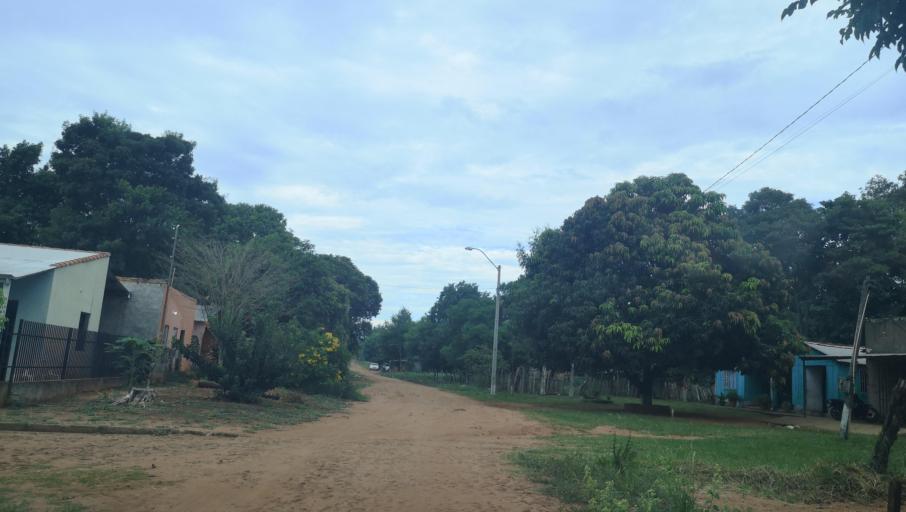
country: PY
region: San Pedro
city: Capiibary
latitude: -24.7347
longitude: -56.0233
